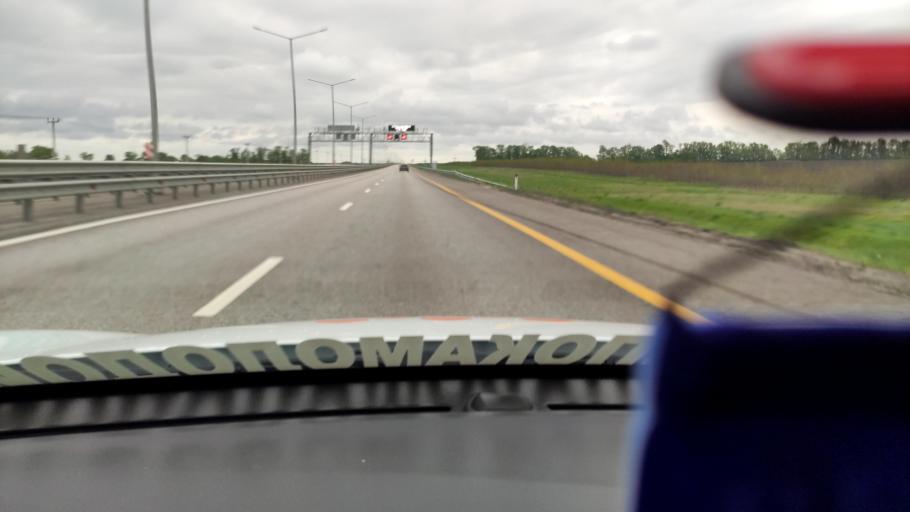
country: RU
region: Voronezj
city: Podkletnoye
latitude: 51.5659
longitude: 39.4768
